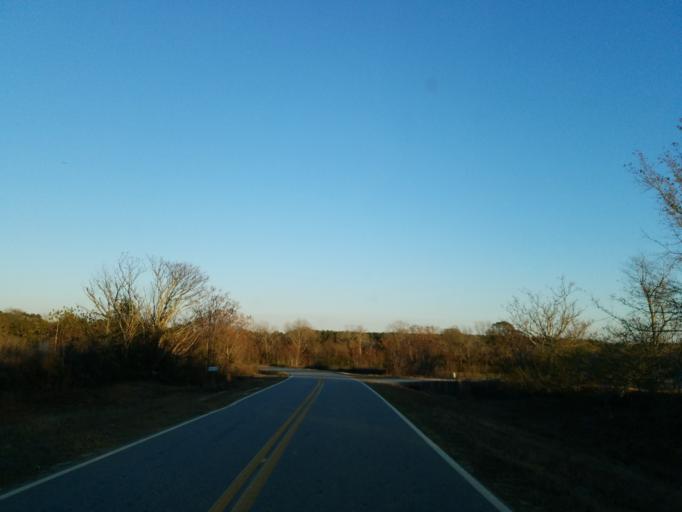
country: US
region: Georgia
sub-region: Turner County
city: Ashburn
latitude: 31.5653
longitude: -83.6877
